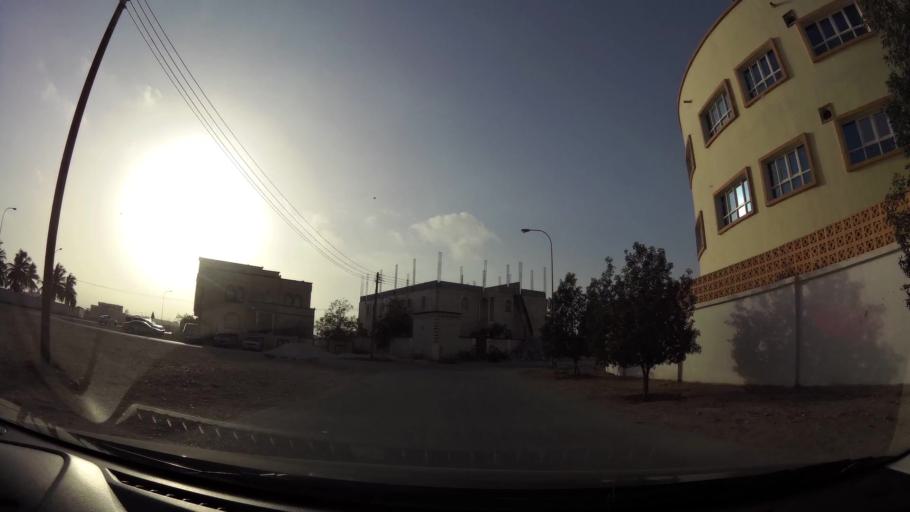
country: OM
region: Zufar
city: Salalah
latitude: 16.9957
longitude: 54.0264
